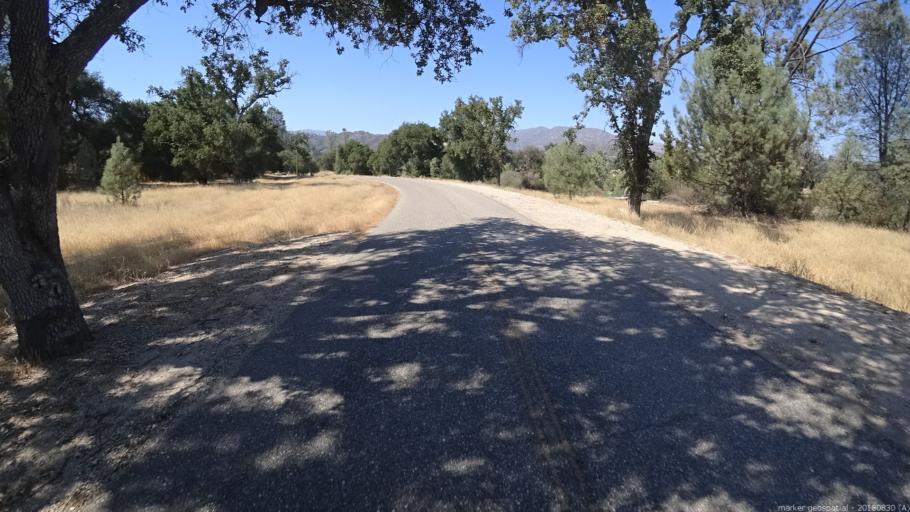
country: US
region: California
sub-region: Monterey County
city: King City
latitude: 36.0593
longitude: -121.3082
